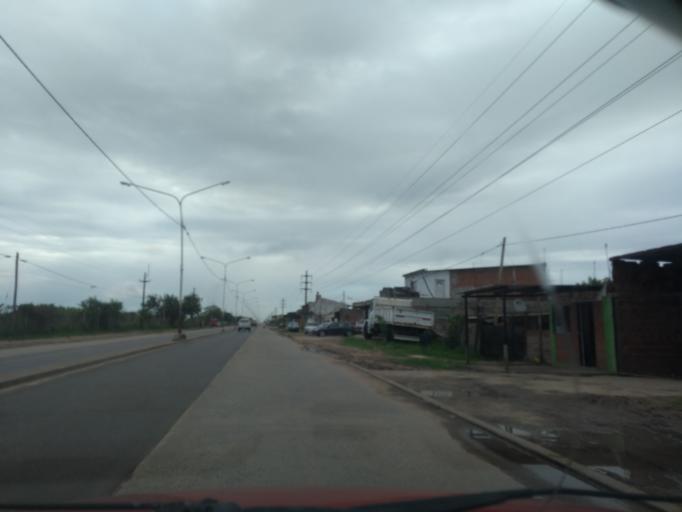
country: AR
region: Chaco
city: Barranqueras
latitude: -27.4855
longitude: -58.9621
